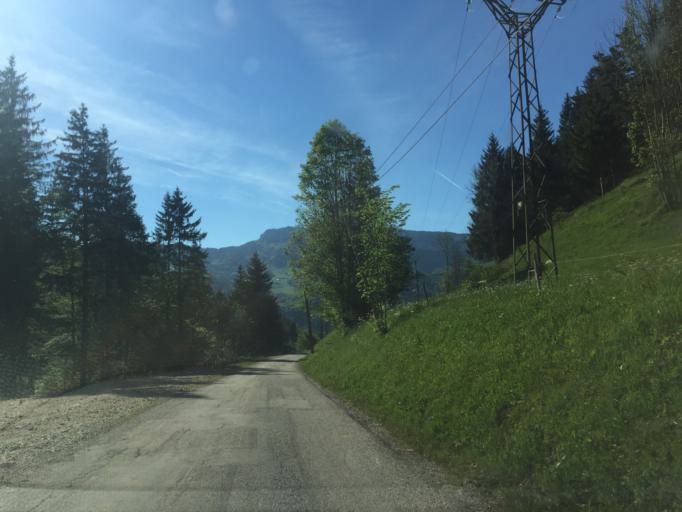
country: FR
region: Rhone-Alpes
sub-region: Departement de l'Isere
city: Barraux
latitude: 45.4445
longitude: 5.8992
